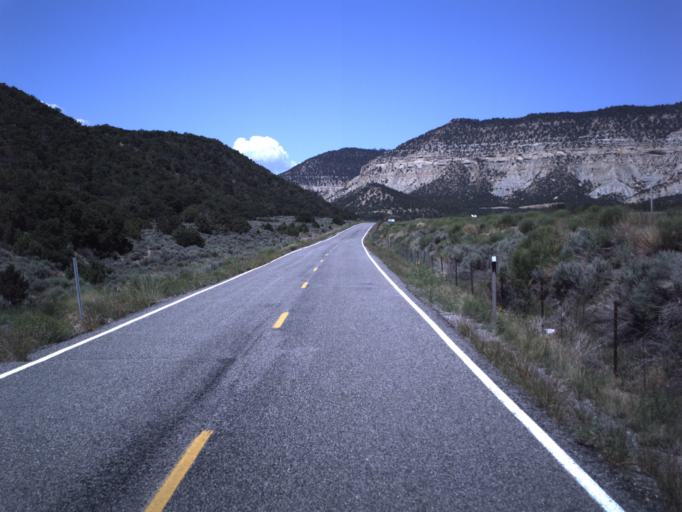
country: US
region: Utah
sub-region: Emery County
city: Ferron
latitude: 38.7556
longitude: -111.3980
